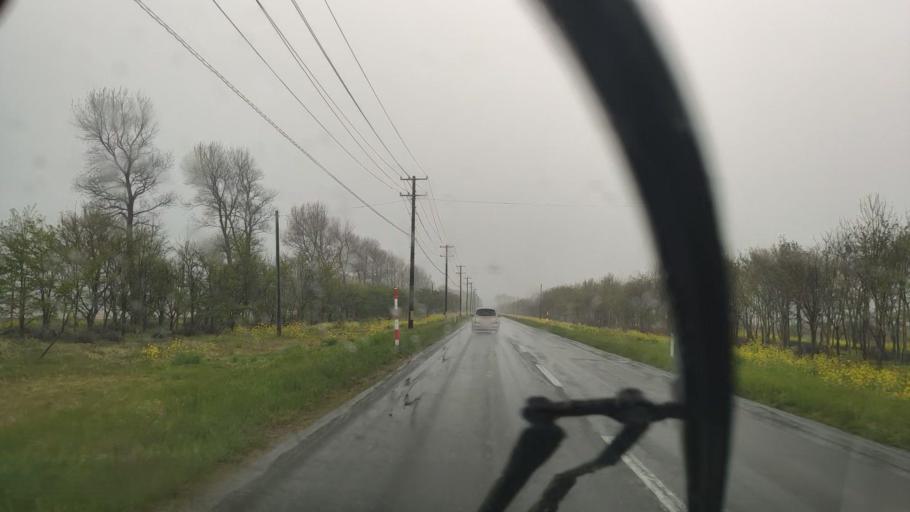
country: JP
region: Akita
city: Tenno
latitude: 39.9619
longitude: 139.9461
